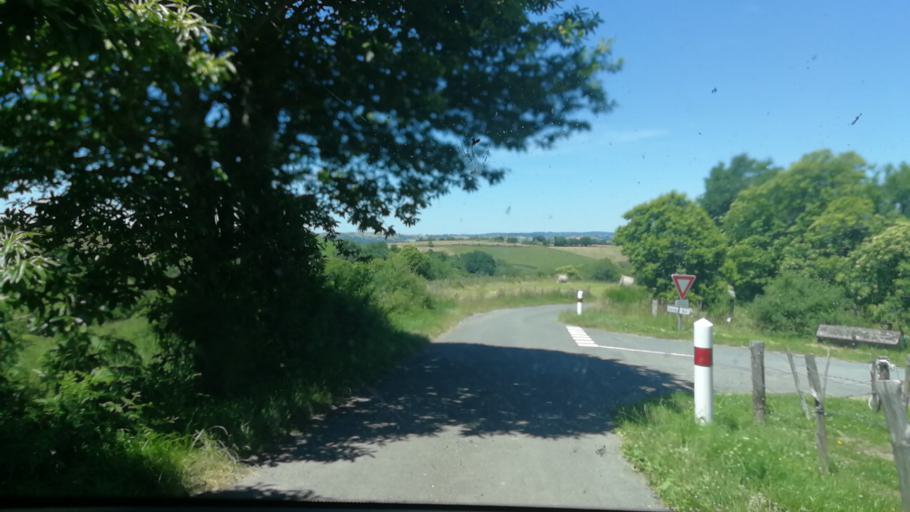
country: FR
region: Midi-Pyrenees
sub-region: Departement de l'Aveyron
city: Firmi
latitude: 44.5818
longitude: 2.3816
